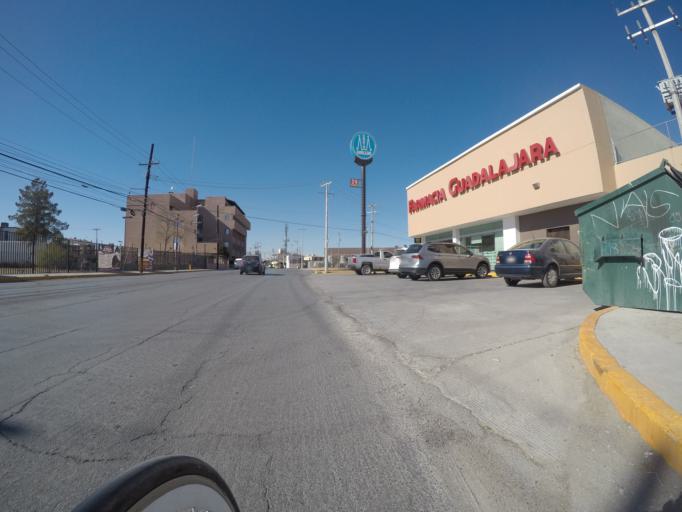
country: MX
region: Chihuahua
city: Ciudad Juarez
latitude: 31.7130
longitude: -106.4149
